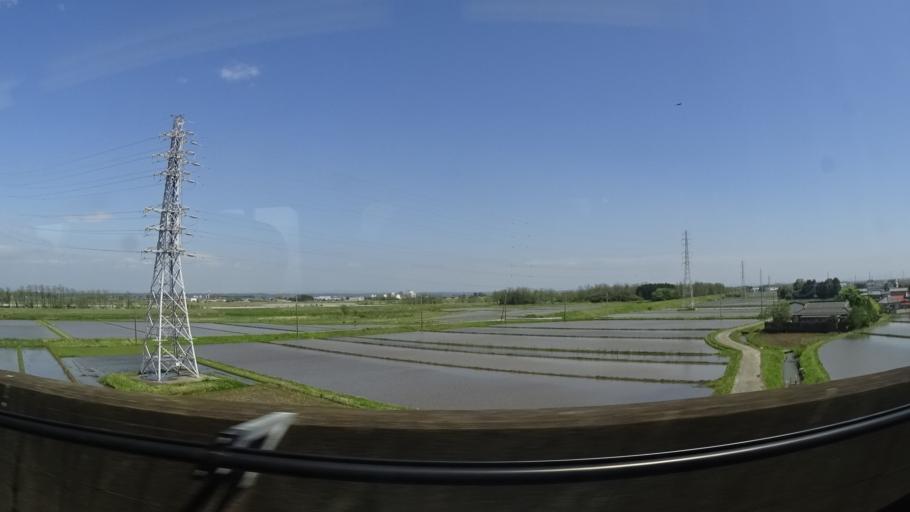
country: JP
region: Tochigi
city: Ujiie
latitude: 36.7010
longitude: 139.9192
